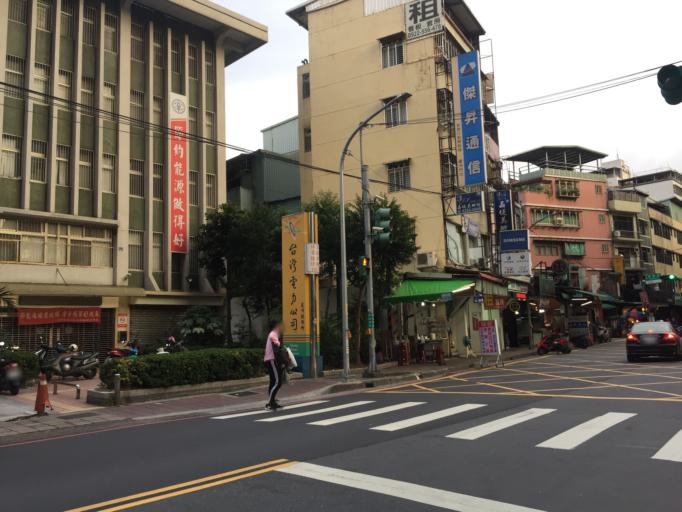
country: TW
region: Taipei
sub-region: Taipei
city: Banqiao
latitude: 25.0830
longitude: 121.4706
